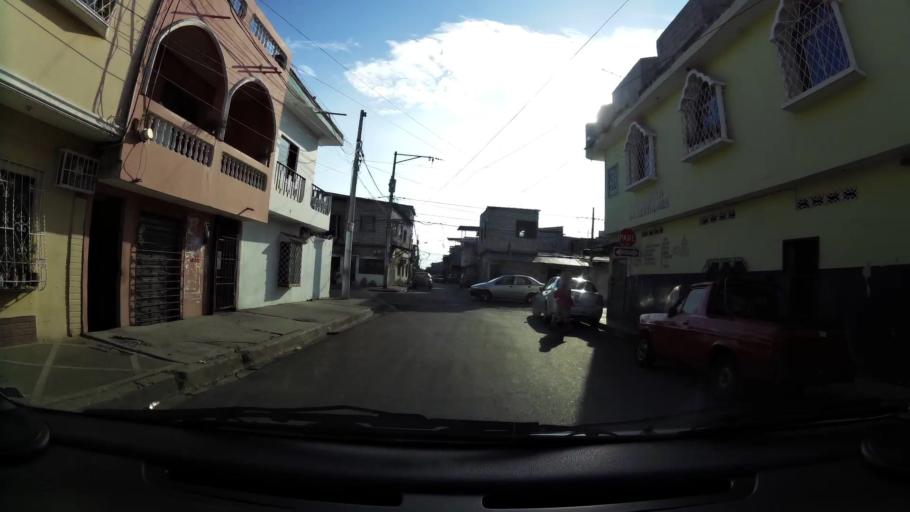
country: EC
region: Guayas
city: Guayaquil
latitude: -2.2273
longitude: -79.9101
